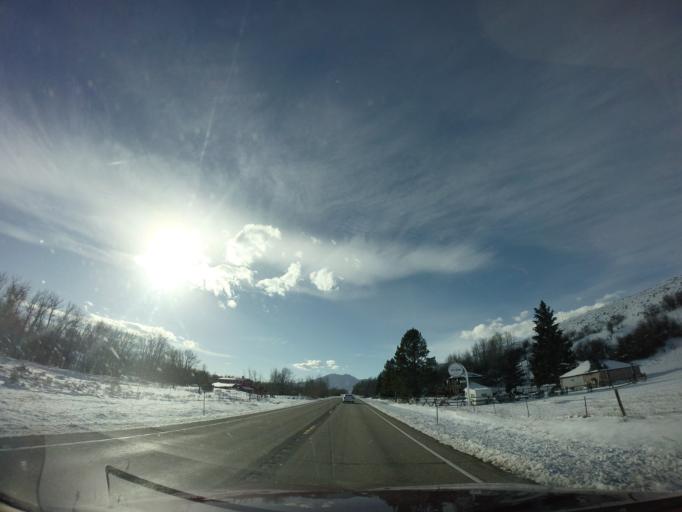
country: US
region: Montana
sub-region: Carbon County
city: Red Lodge
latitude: 45.2312
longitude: -109.2384
